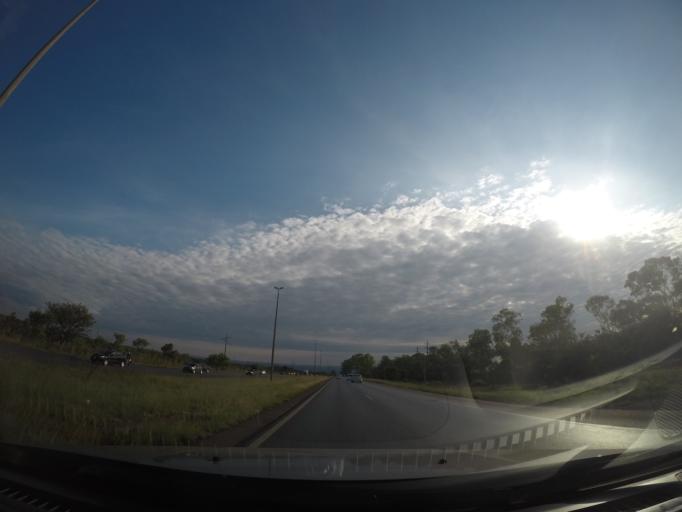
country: BR
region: Goias
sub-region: Planaltina
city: Planaltina
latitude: -15.6287
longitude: -47.7301
